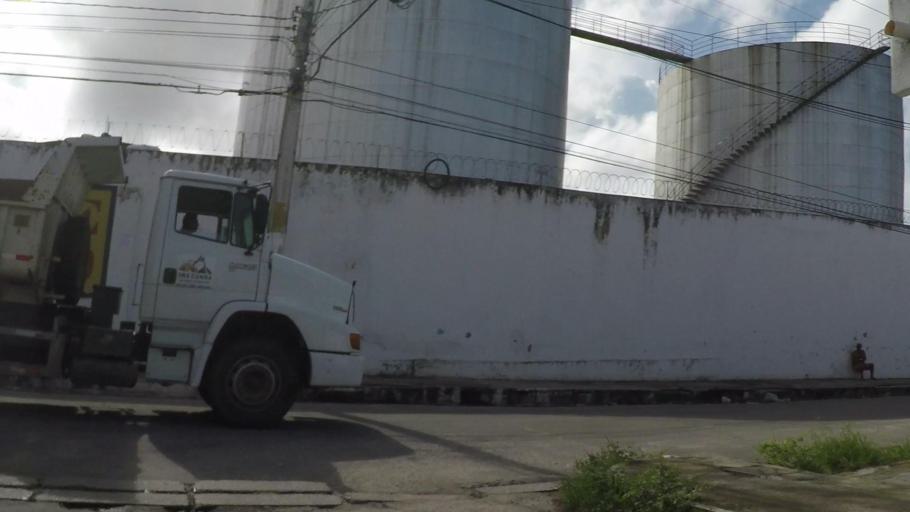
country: BR
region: Ceara
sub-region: Fortaleza
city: Fortaleza
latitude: -3.7397
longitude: -38.5837
